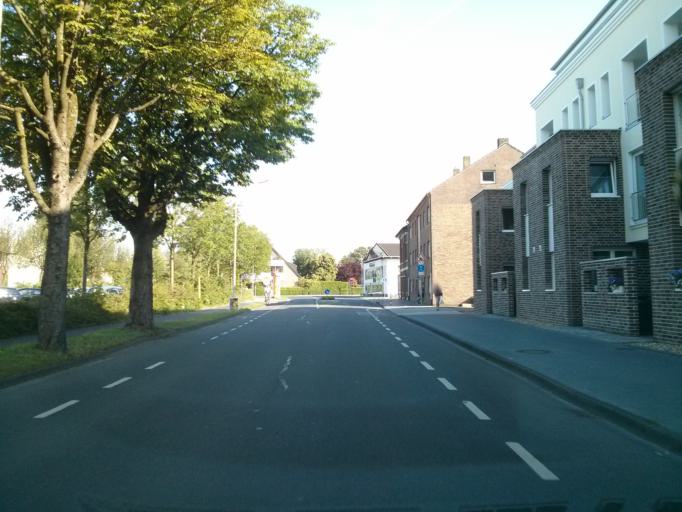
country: DE
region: North Rhine-Westphalia
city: Kempen
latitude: 51.3667
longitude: 6.4257
